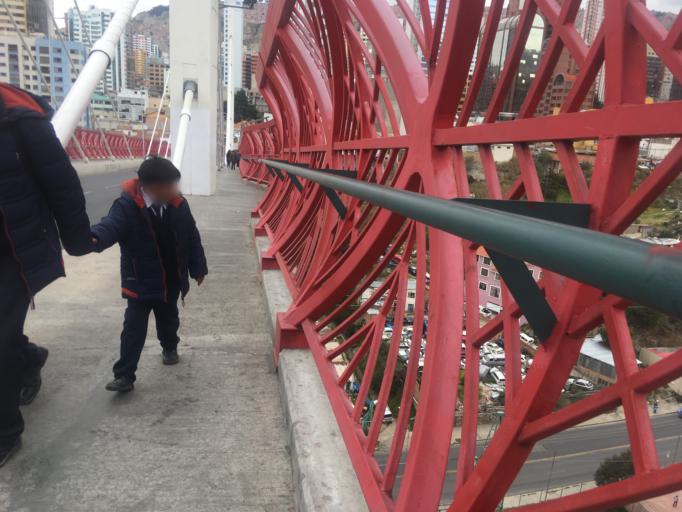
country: BO
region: La Paz
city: La Paz
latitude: -16.5062
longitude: -68.1234
